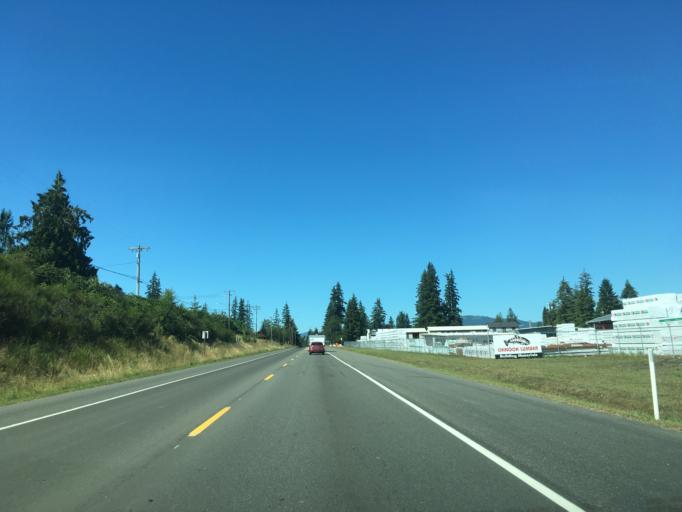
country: US
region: Washington
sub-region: Snohomish County
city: Arlington
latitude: 48.1845
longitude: -122.1287
